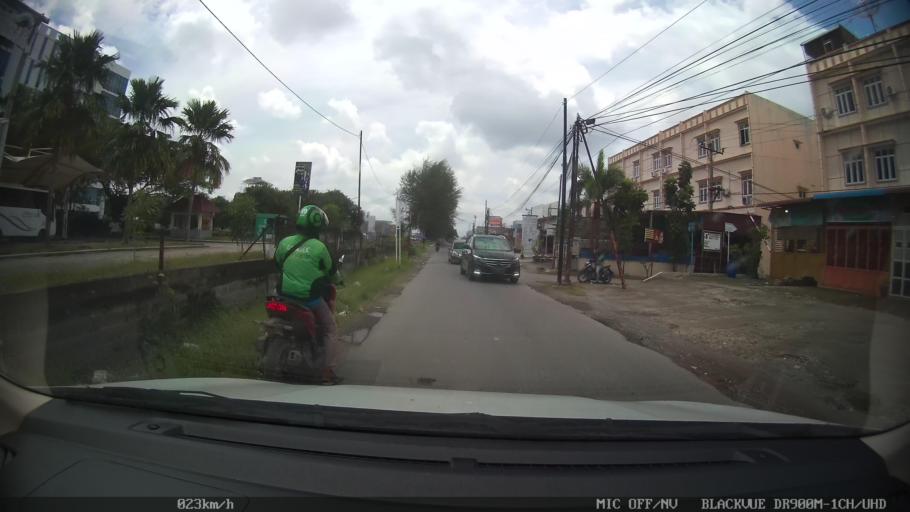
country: ID
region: North Sumatra
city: Medan
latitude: 3.6144
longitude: 98.7292
